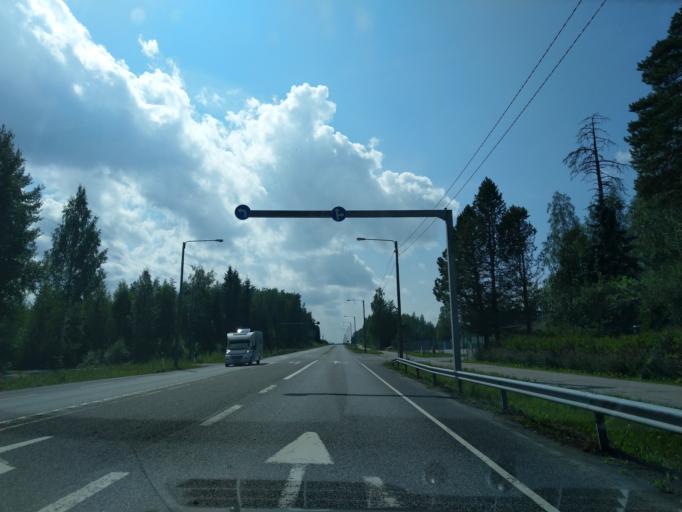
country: FI
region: South Karelia
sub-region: Imatra
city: Ruokolahti
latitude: 61.2661
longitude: 28.9231
